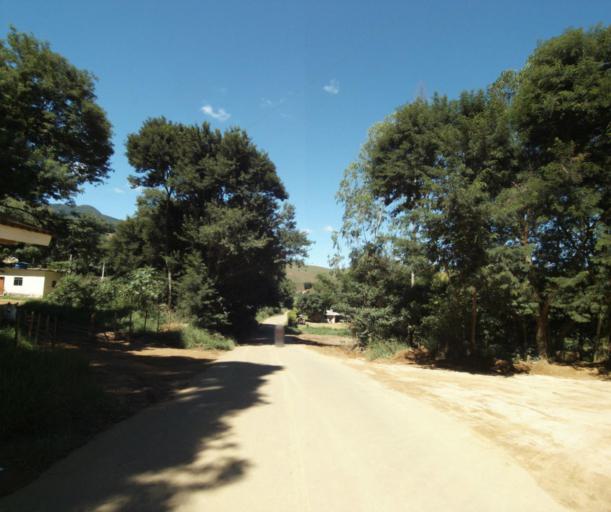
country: BR
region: Minas Gerais
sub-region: Espera Feliz
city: Espera Feliz
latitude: -20.5690
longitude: -41.8302
